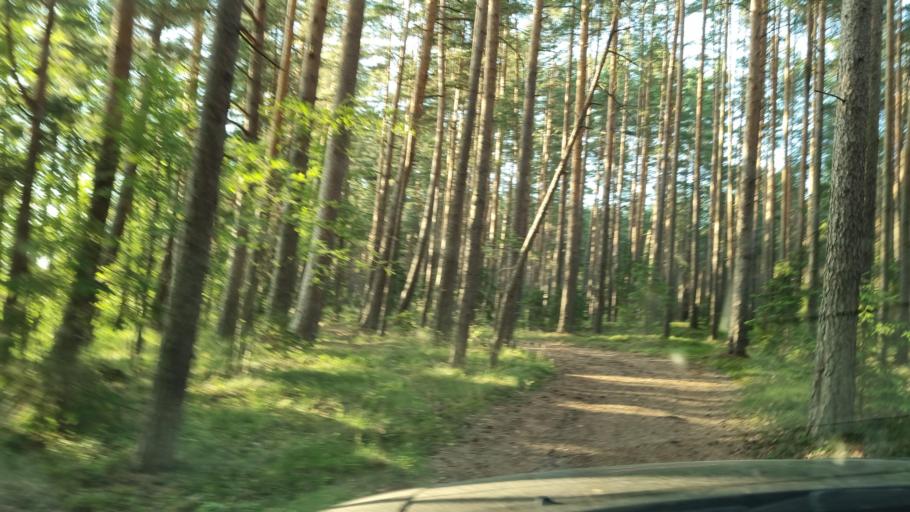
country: LV
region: Kuldigas Rajons
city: Kuldiga
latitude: 57.1916
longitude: 22.1834
